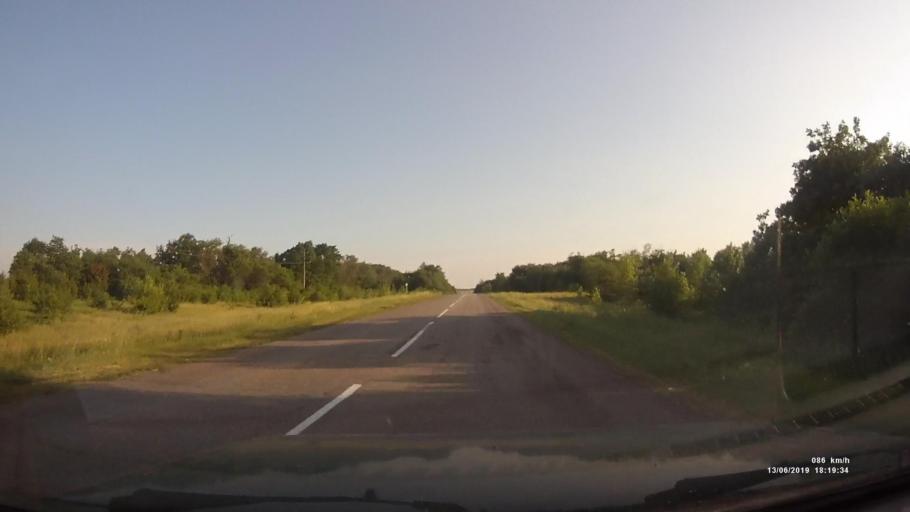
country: RU
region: Rostov
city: Kazanskaya
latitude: 49.8943
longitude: 41.3055
